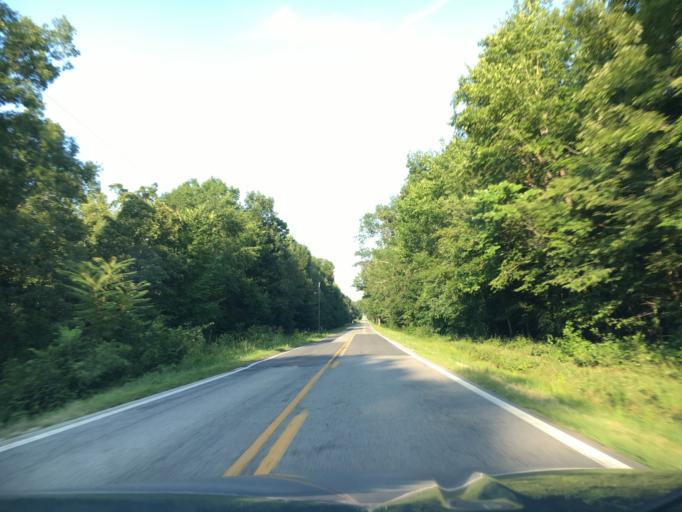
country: US
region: Virginia
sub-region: Pittsylvania County
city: Chatham
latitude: 36.8280
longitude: -79.3073
